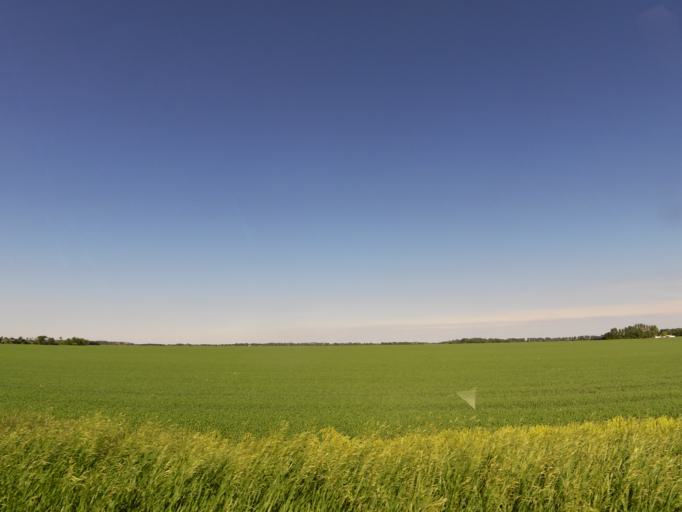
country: US
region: North Dakota
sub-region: Walsh County
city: Grafton
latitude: 48.4004
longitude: -97.2556
